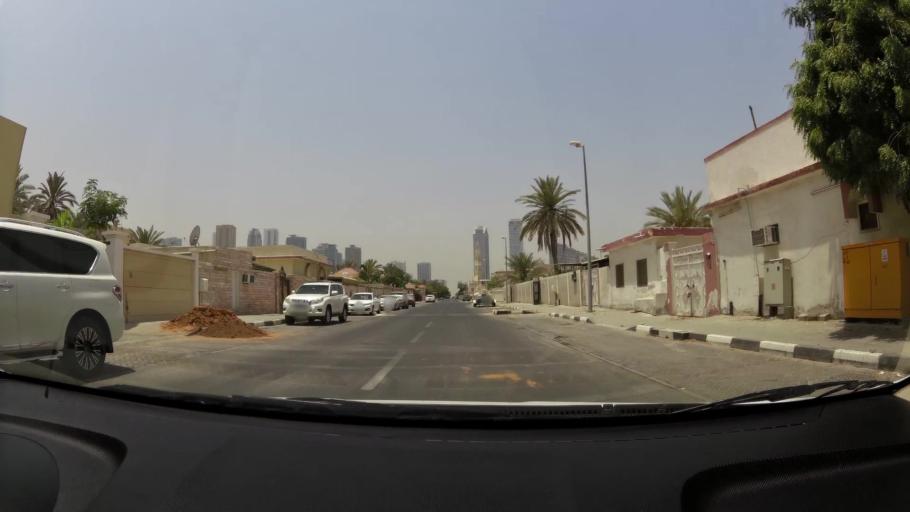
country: AE
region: Ash Shariqah
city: Sharjah
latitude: 25.3377
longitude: 55.3721
